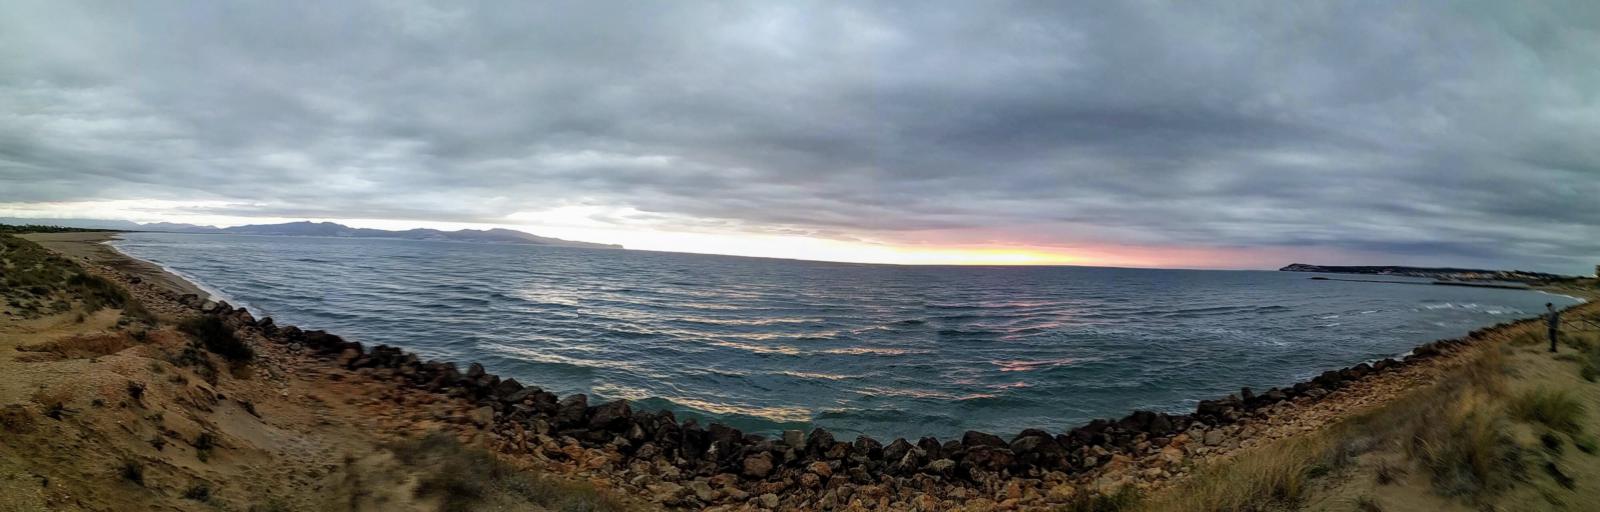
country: ES
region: Catalonia
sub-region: Provincia de Girona
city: l'Escala
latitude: 42.1436
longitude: 3.1172
